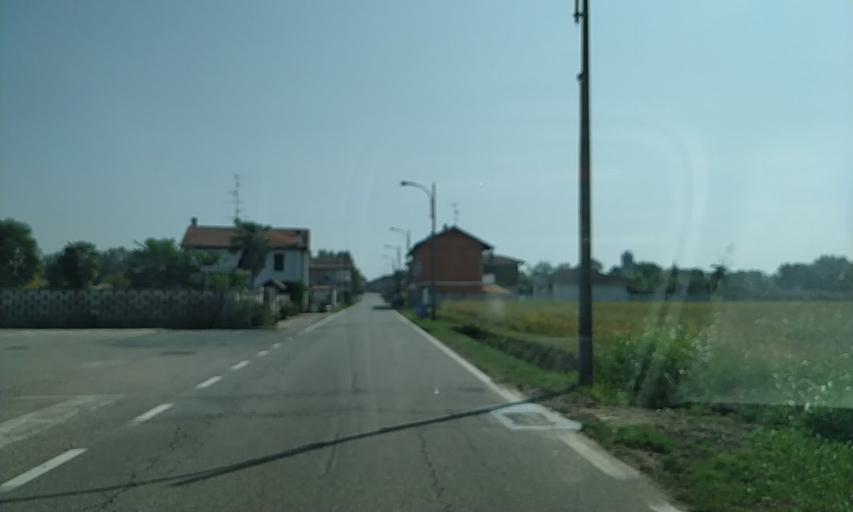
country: IT
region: Piedmont
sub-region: Provincia di Vercelli
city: Crova
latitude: 45.3330
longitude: 8.2043
